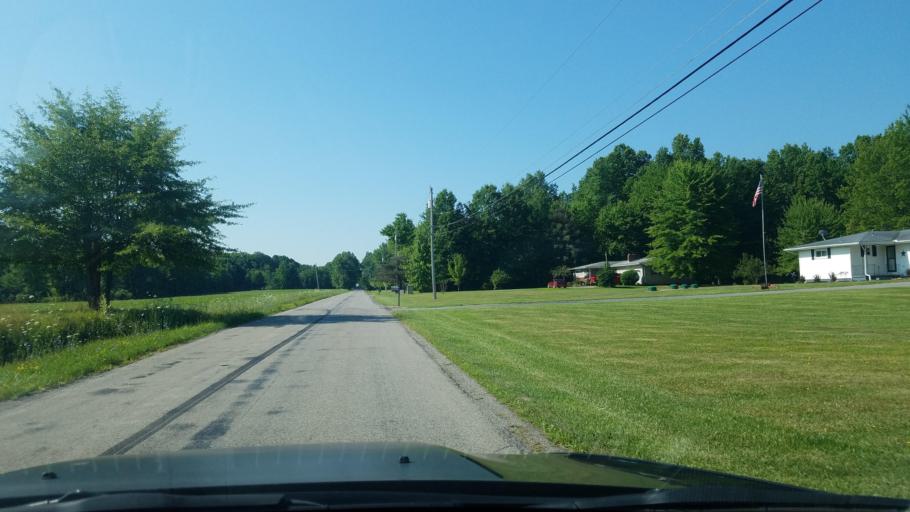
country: US
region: Ohio
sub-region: Trumbull County
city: Leavittsburg
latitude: 41.2993
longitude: -80.9058
